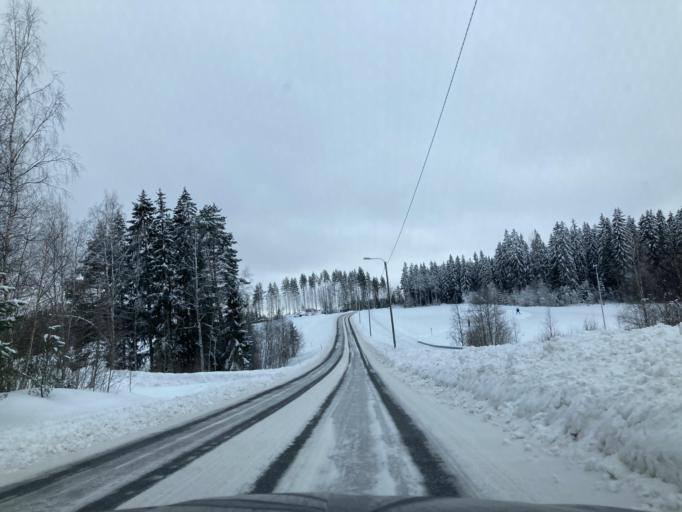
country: FI
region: Central Finland
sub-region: Jaemsae
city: Jaemsae
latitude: 61.8717
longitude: 25.2667
